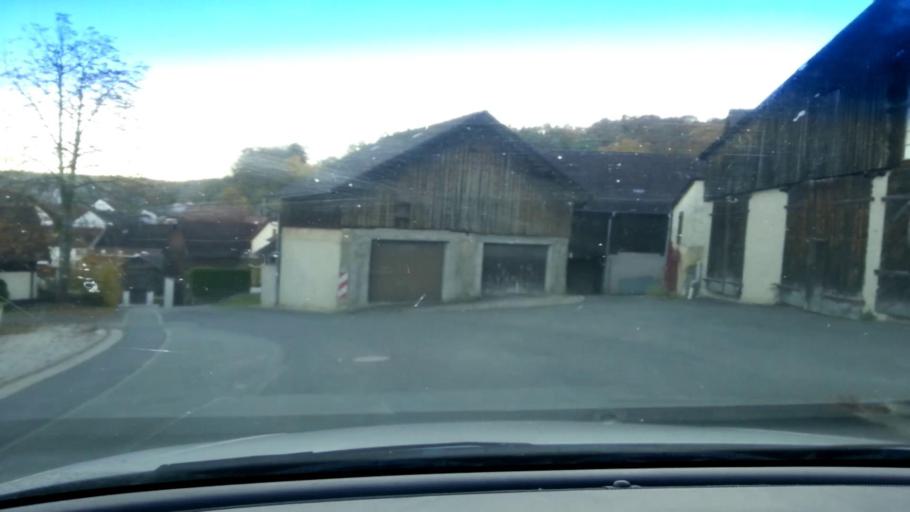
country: DE
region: Bavaria
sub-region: Upper Franconia
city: Heiligenstadt
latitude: 49.8366
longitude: 11.1580
